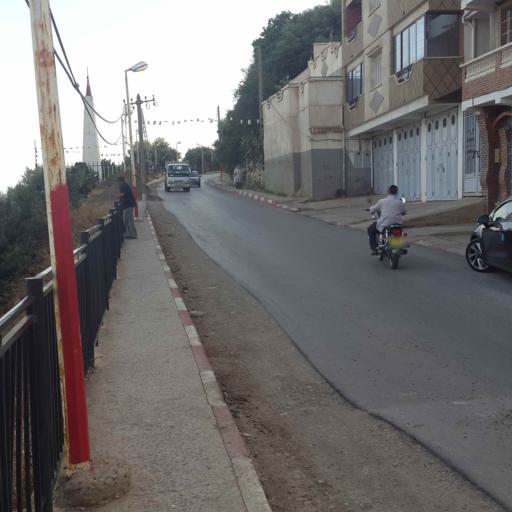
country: DZ
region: Tizi Ouzou
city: Chemini
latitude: 36.6051
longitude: 4.6385
